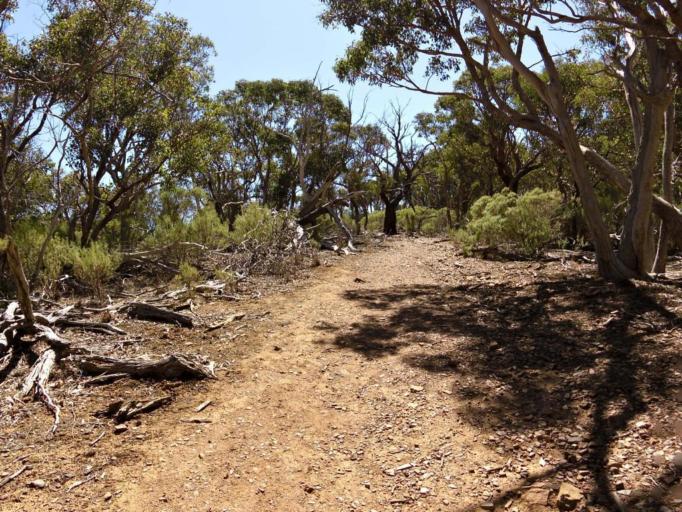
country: AU
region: Victoria
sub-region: Moorabool
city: Bacchus Marsh
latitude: -37.6576
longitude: 144.3493
